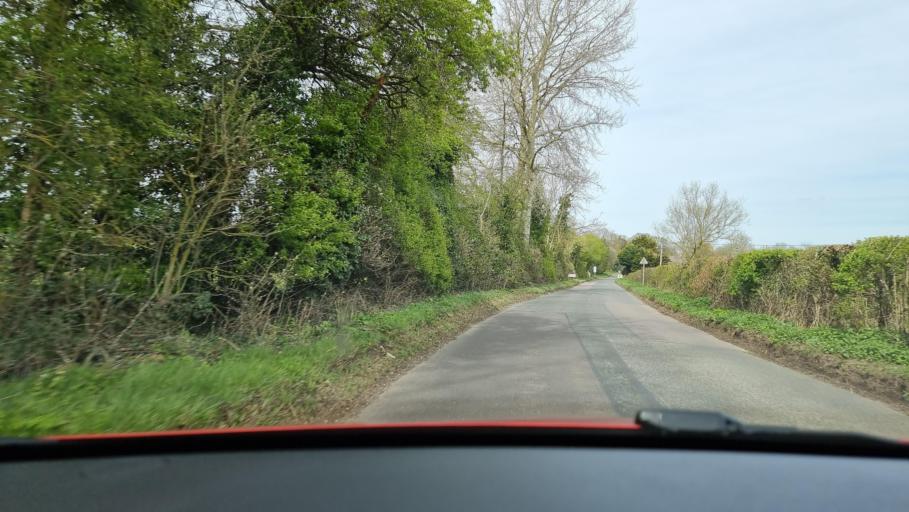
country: GB
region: England
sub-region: Oxfordshire
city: Oxford
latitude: 51.7998
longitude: -1.2261
